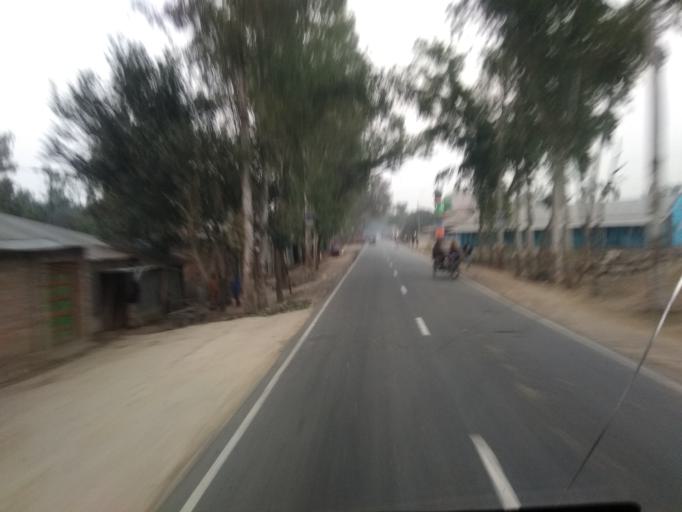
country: BD
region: Rajshahi
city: Bogra
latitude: 24.6768
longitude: 89.2837
